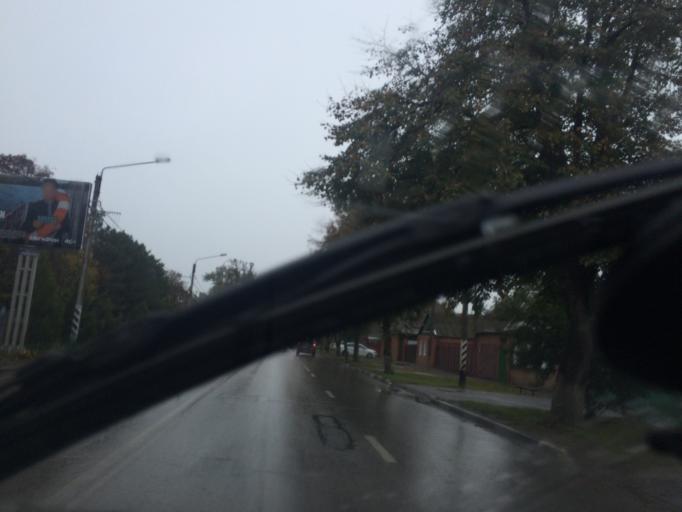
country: RU
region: Rostov
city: Azov
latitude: 47.1000
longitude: 39.4402
